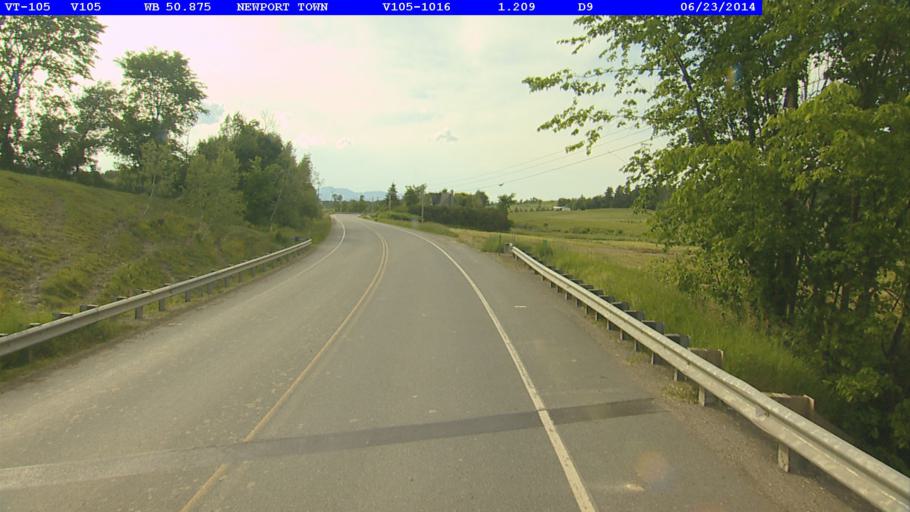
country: US
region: Vermont
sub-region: Orleans County
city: Newport
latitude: 44.9690
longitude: -72.3157
